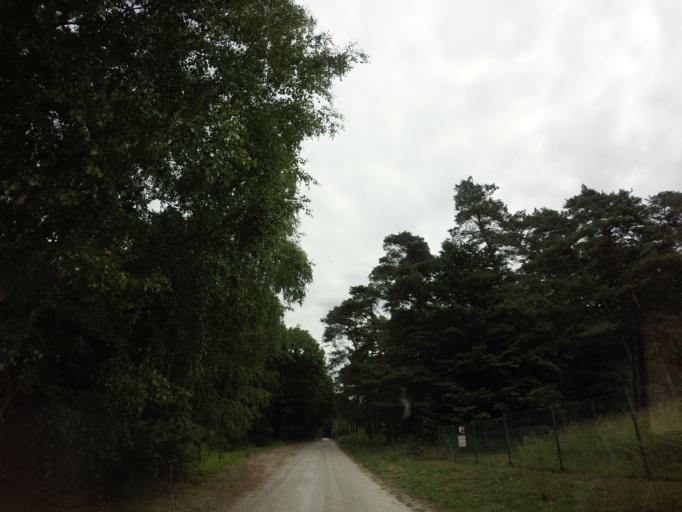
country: PL
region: Lubusz
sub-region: Powiat strzelecko-drezdenecki
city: Stare Kurowo
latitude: 52.9011
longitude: 15.6594
